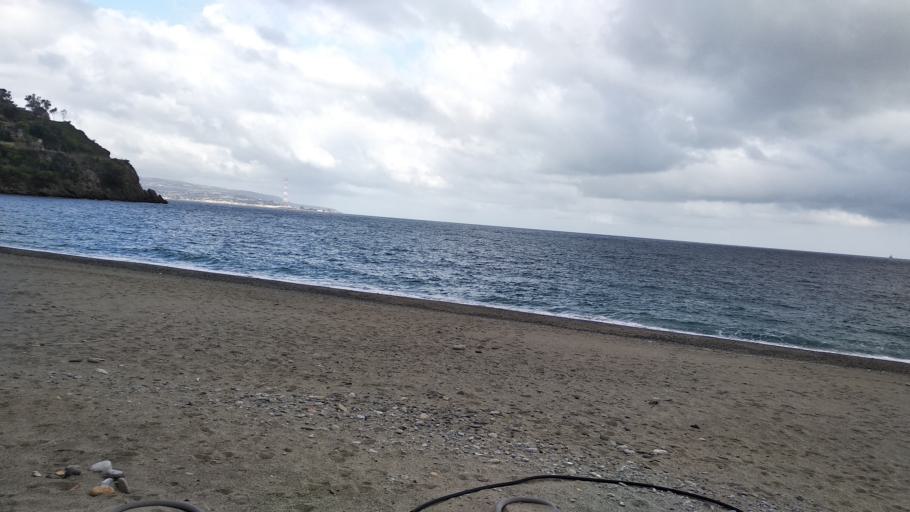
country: IT
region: Calabria
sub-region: Provincia di Reggio Calabria
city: Scilla
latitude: 38.2522
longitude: 15.7106
